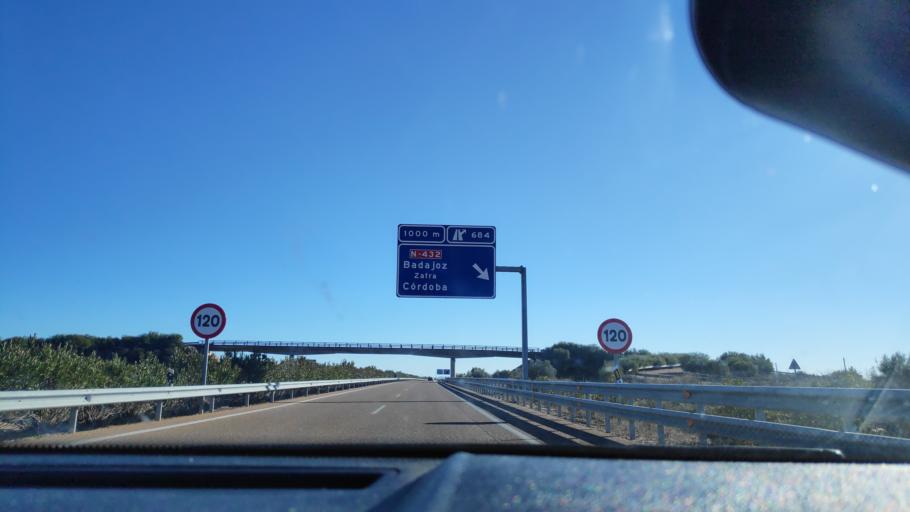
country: ES
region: Extremadura
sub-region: Provincia de Badajoz
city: Los Santos de Maimona
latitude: 38.4119
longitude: -6.3427
